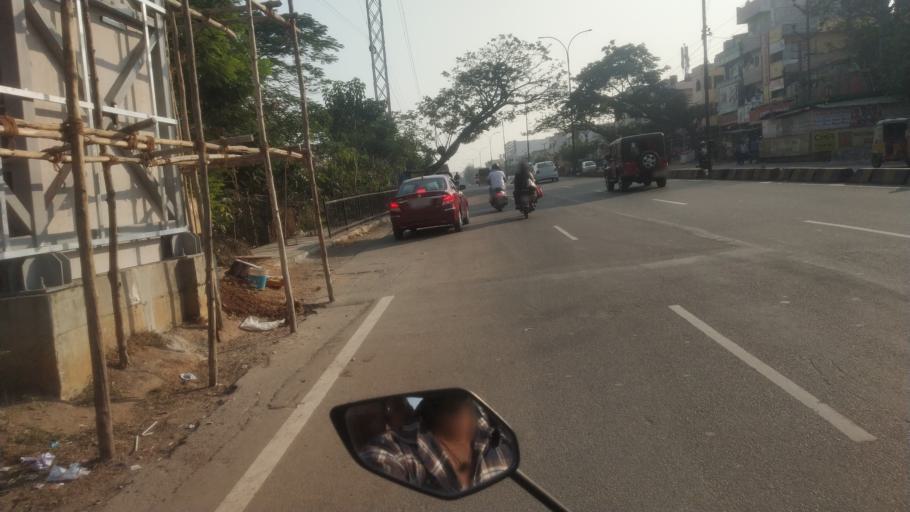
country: IN
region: Telangana
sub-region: Rangareddi
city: Quthbullapur
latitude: 17.4873
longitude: 78.4502
